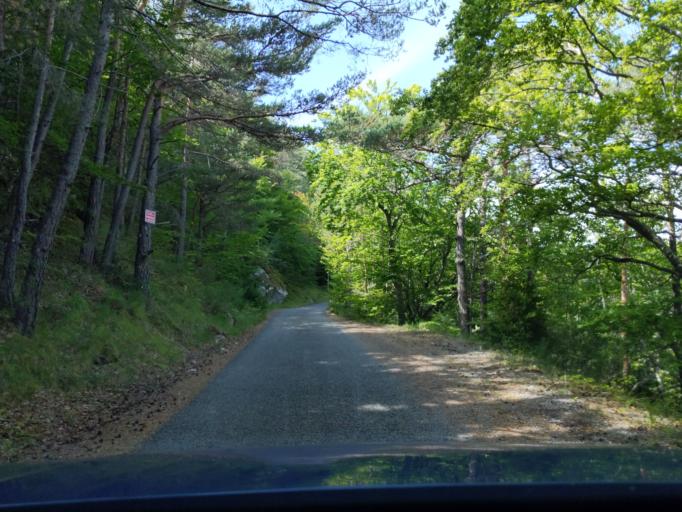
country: FR
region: Provence-Alpes-Cote d'Azur
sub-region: Departement des Hautes-Alpes
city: Veynes
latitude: 44.6312
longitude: 5.6840
